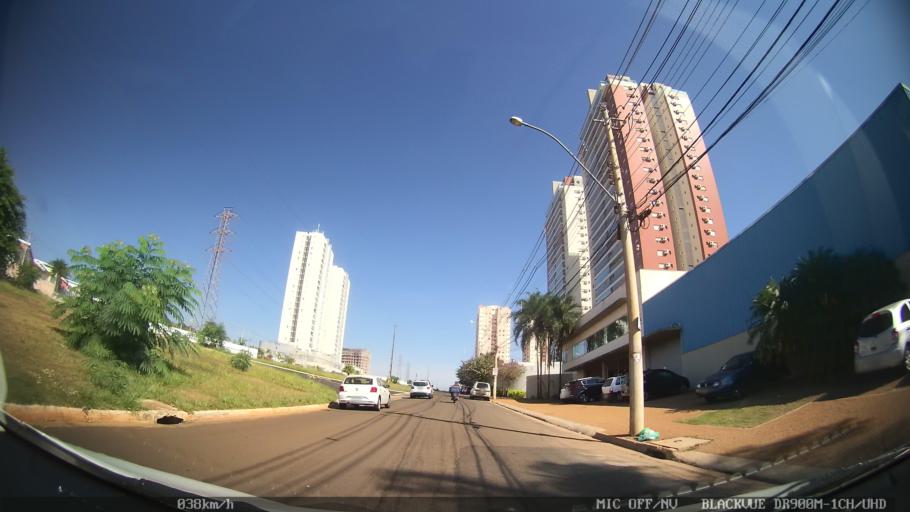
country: BR
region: Sao Paulo
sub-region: Ribeirao Preto
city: Ribeirao Preto
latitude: -21.2191
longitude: -47.7938
